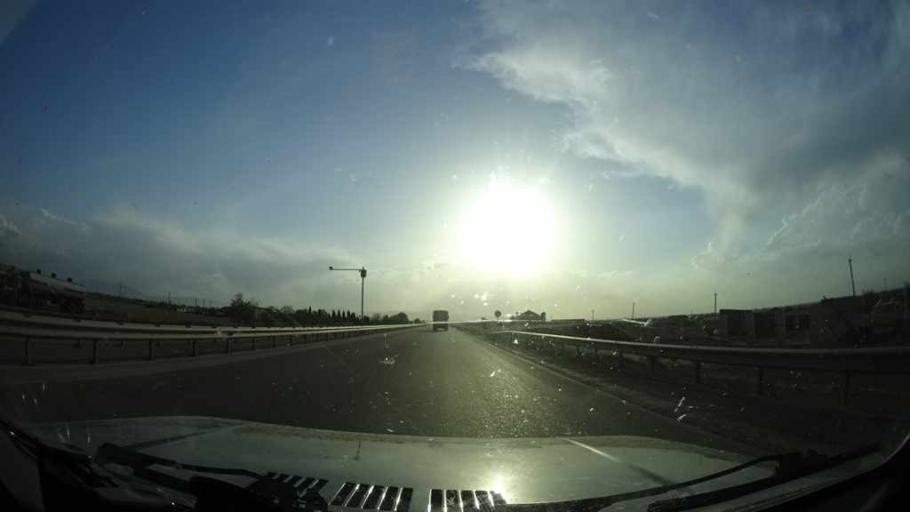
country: AZ
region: Samux
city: Samux
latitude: 40.6895
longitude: 46.5467
